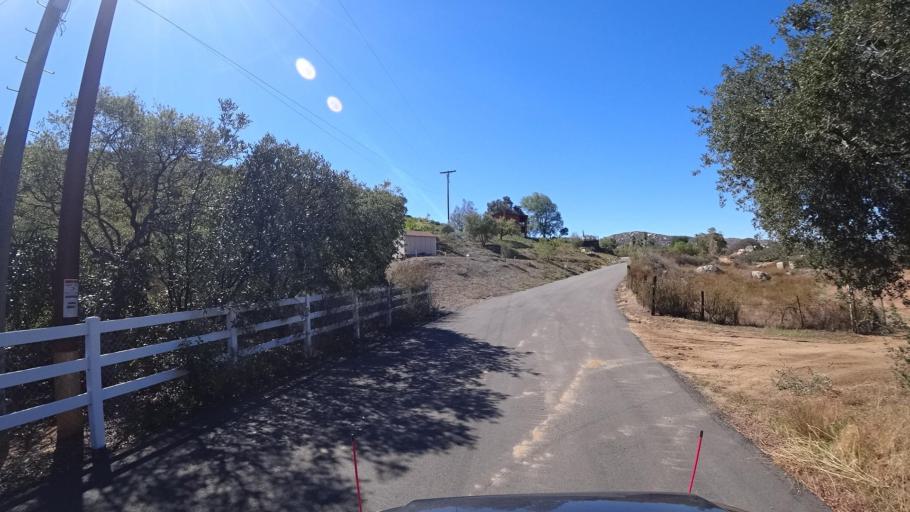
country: US
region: California
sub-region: San Diego County
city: Alpine
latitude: 32.7693
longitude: -116.6998
